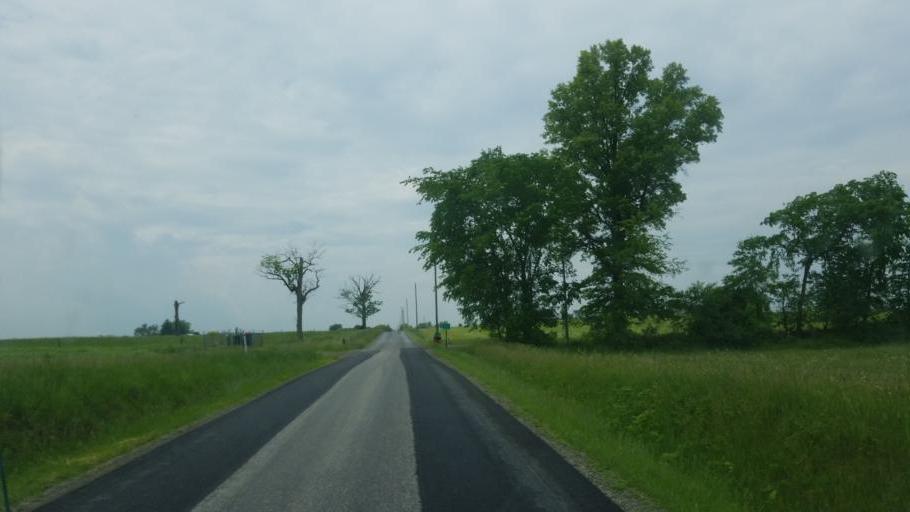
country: US
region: Ohio
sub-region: Wayne County
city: Orrville
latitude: 40.7824
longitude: -81.7646
